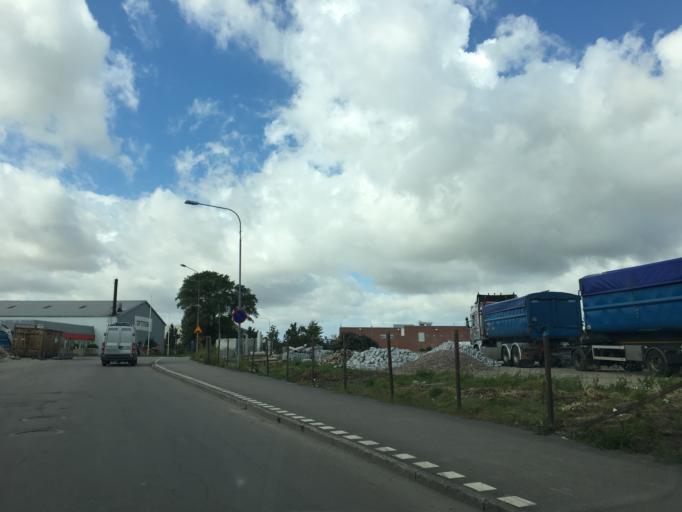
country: SE
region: Skane
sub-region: Svedala Kommun
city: Svedala
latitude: 55.5062
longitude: 13.2373
